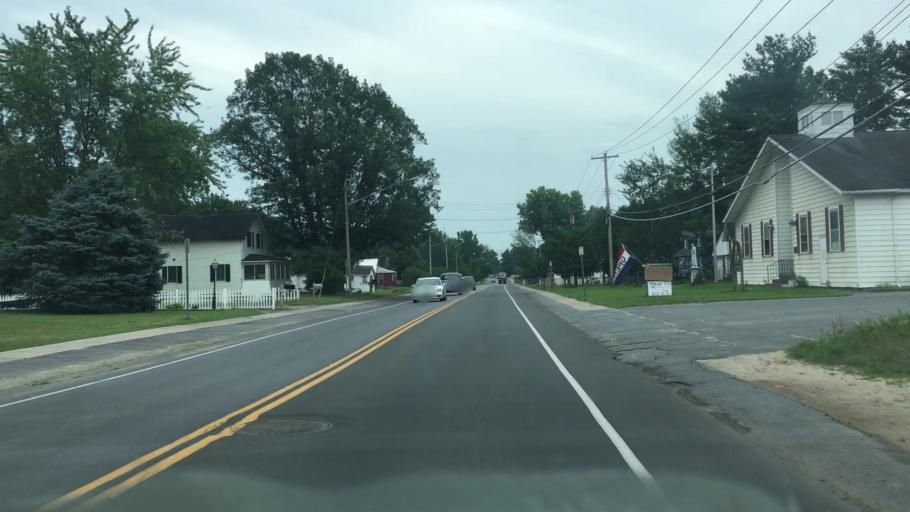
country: US
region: New York
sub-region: Clinton County
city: Plattsburgh West
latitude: 44.6811
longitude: -73.5063
